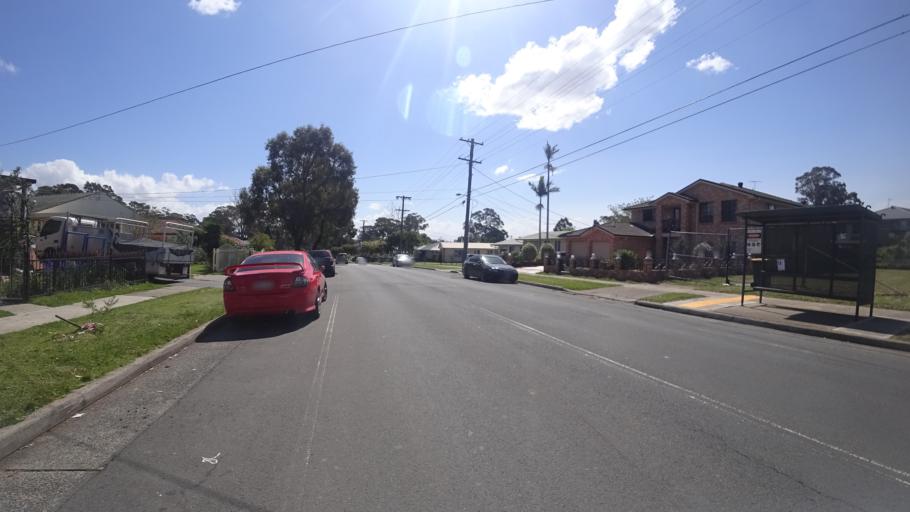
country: AU
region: New South Wales
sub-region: Liverpool
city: Miller
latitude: -33.9097
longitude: 150.8931
